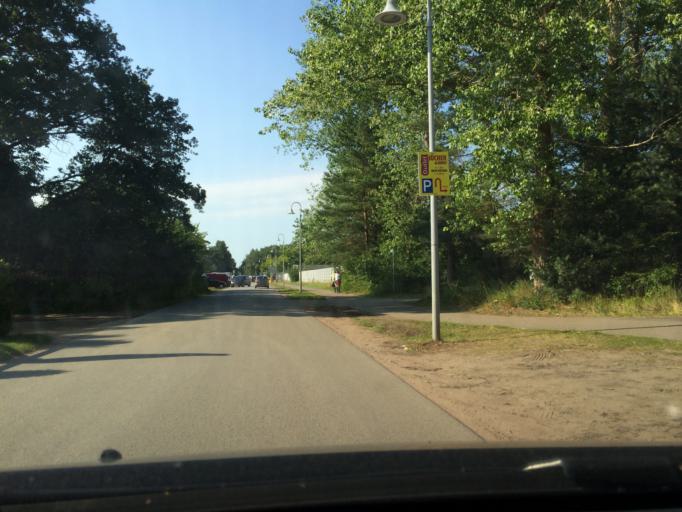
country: DE
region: Mecklenburg-Vorpommern
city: Ostseebad Binz
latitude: 54.4407
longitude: 13.5674
